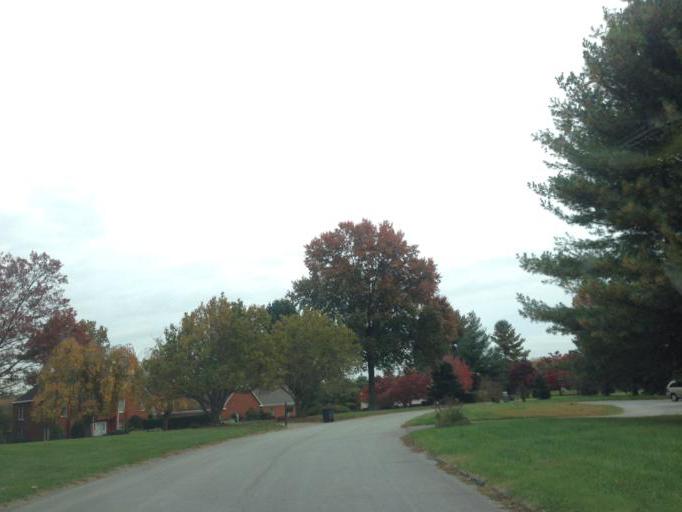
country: US
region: Maryland
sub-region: Howard County
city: Highland
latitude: 39.2723
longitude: -76.9319
